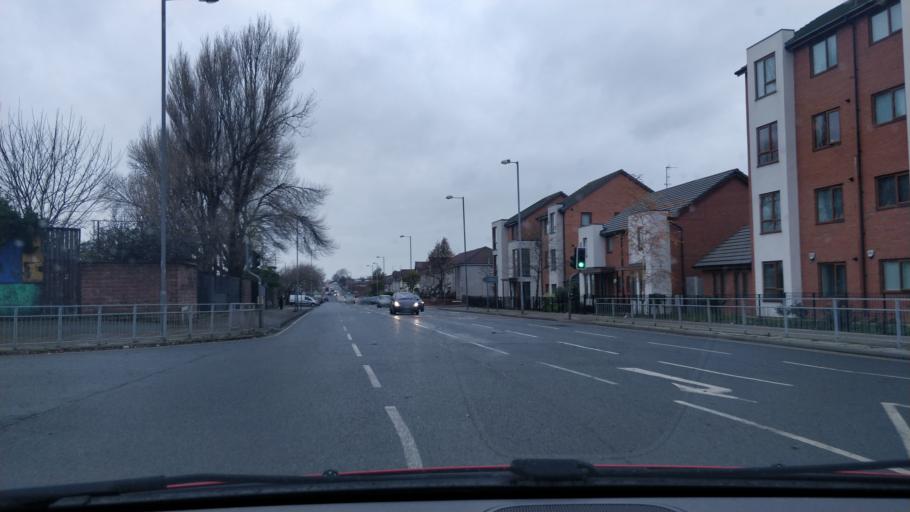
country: GB
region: England
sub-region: Sefton
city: Litherland
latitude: 53.4598
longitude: -2.9856
